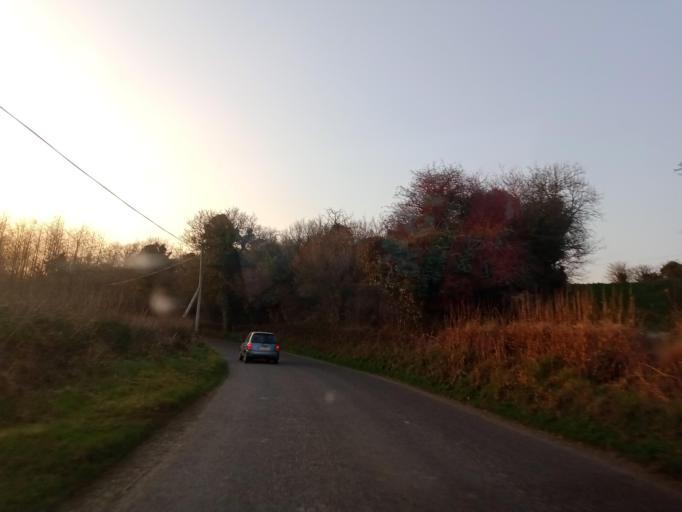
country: IE
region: Leinster
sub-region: Kilkenny
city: Castlecomer
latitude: 52.8625
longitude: -7.2698
